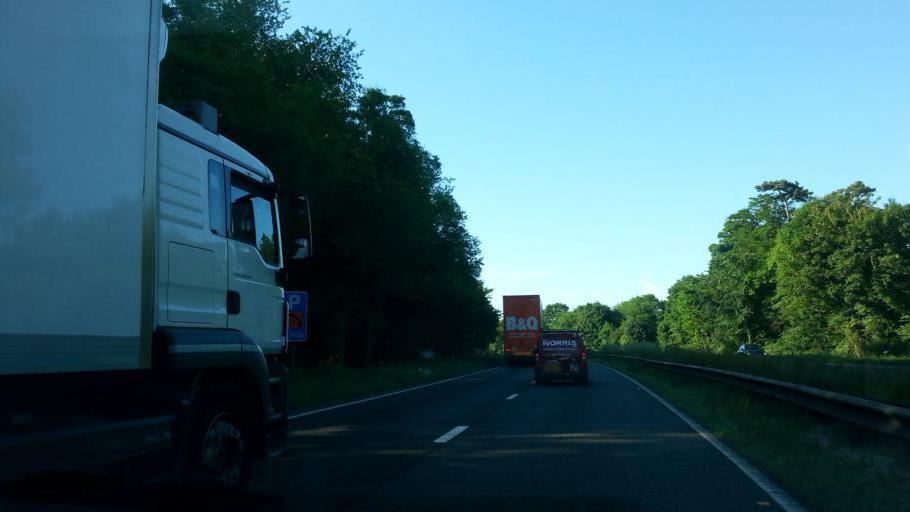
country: GB
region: England
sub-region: Lincolnshire
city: Grantham
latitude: 52.8301
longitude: -0.6313
